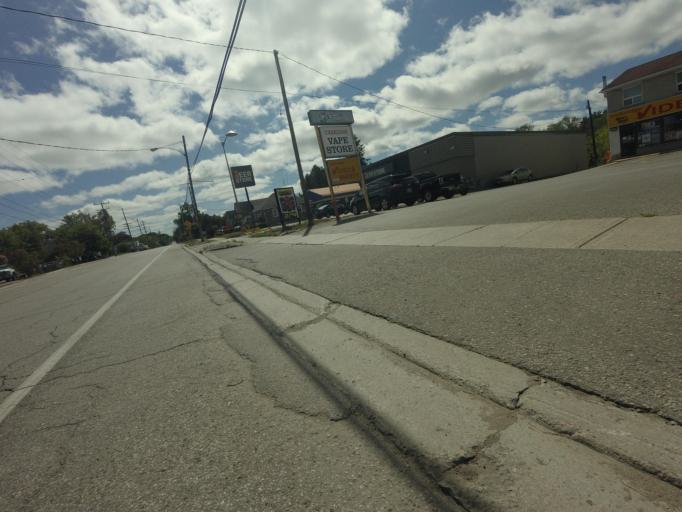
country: CA
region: Ontario
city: Uxbridge
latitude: 44.1154
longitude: -79.1233
